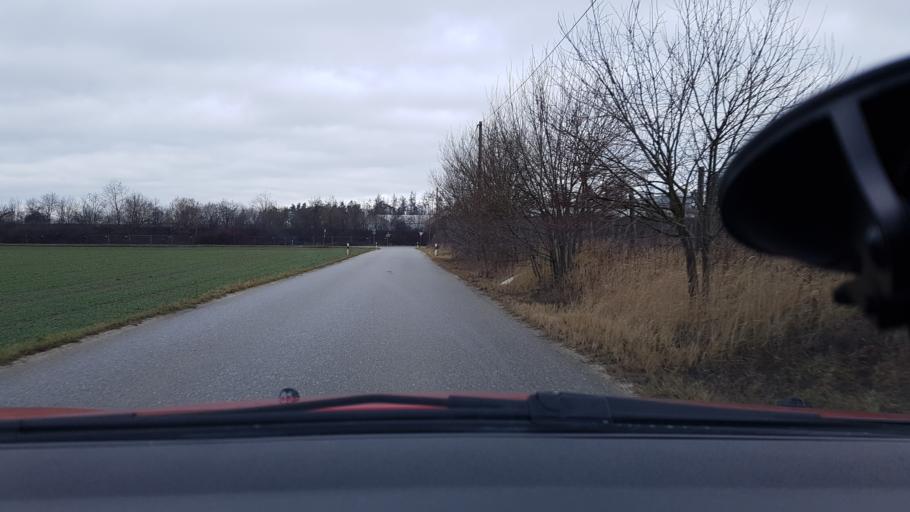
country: DE
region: Bavaria
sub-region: Upper Bavaria
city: Altoetting
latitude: 48.2385
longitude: 12.6693
